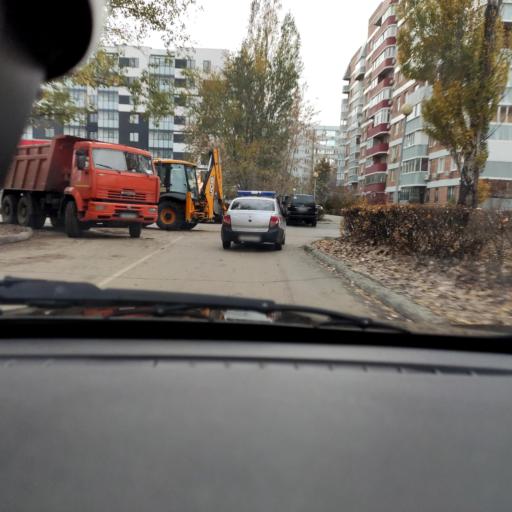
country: RU
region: Samara
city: Tol'yatti
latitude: 53.5338
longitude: 49.2895
